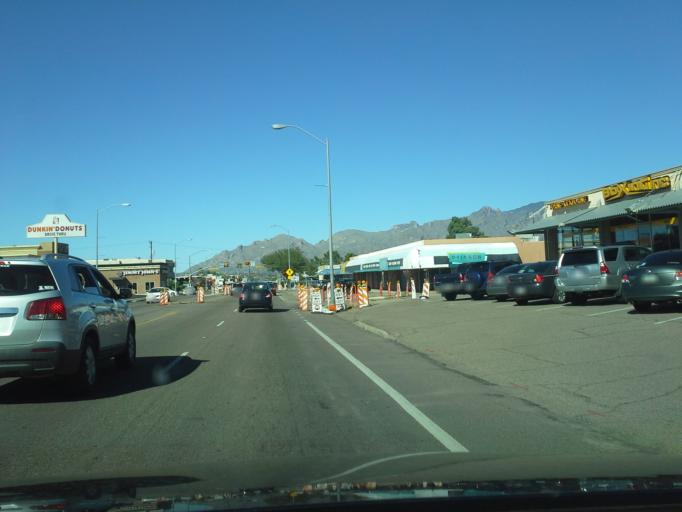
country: US
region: Arizona
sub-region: Pima County
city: Tucson
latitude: 32.2526
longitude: -110.9439
